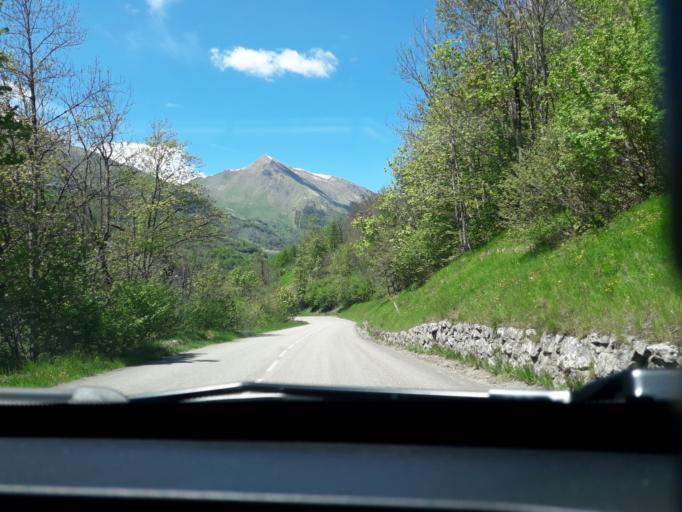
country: FR
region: Rhone-Alpes
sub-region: Departement de la Savoie
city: Saint-Martin-de-Belleville
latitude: 45.4019
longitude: 6.4938
